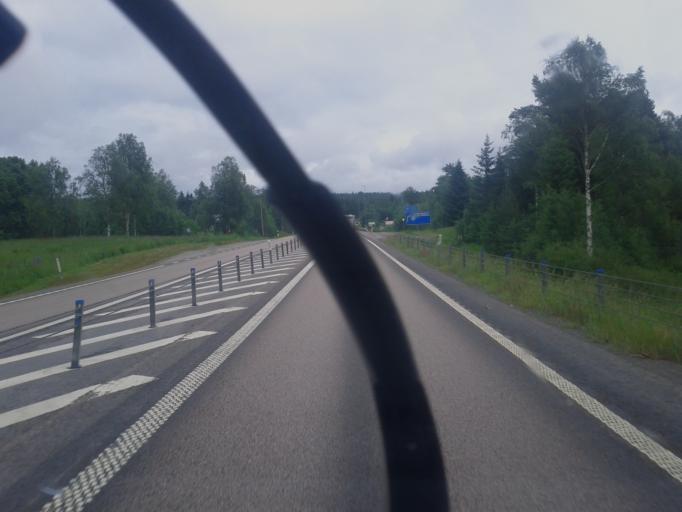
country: SE
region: Vaesternorrland
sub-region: Timra Kommun
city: Soraker
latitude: 62.5546
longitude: 17.6392
